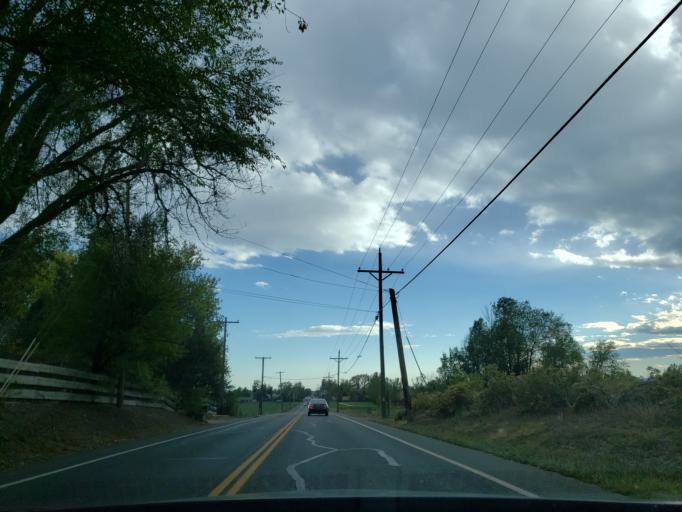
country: US
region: Colorado
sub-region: Larimer County
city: Fort Collins
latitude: 40.6009
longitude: -105.0294
